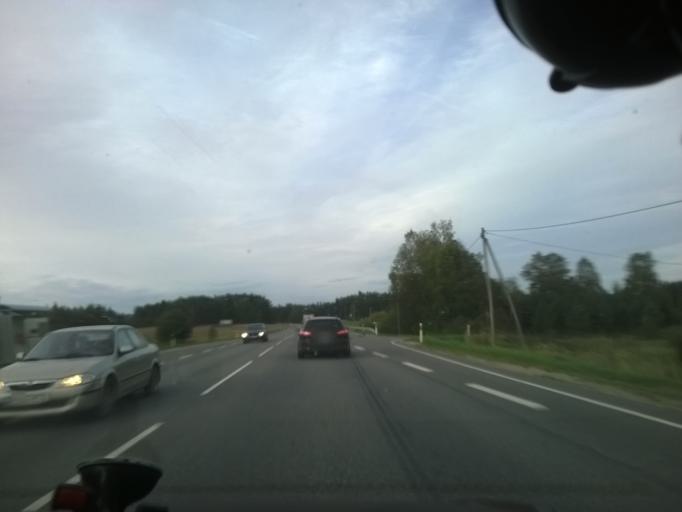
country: EE
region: Tartu
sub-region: UElenurme vald
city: Ulenurme
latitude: 58.0923
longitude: 26.7363
